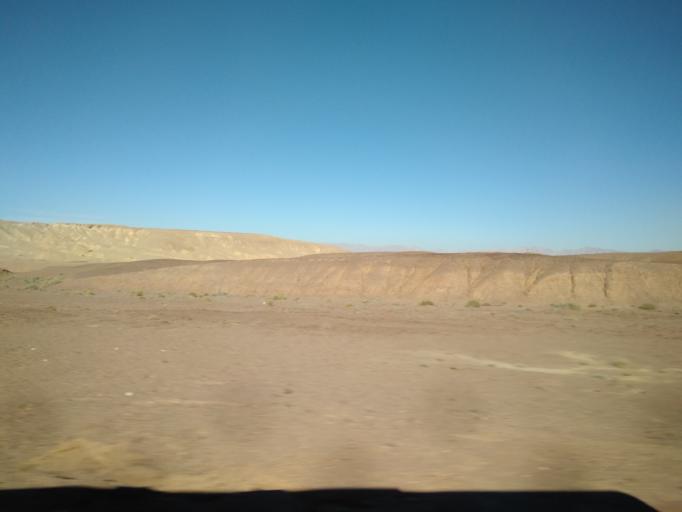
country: IL
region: Southern District
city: Eilat
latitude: 29.6751
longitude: 34.8679
